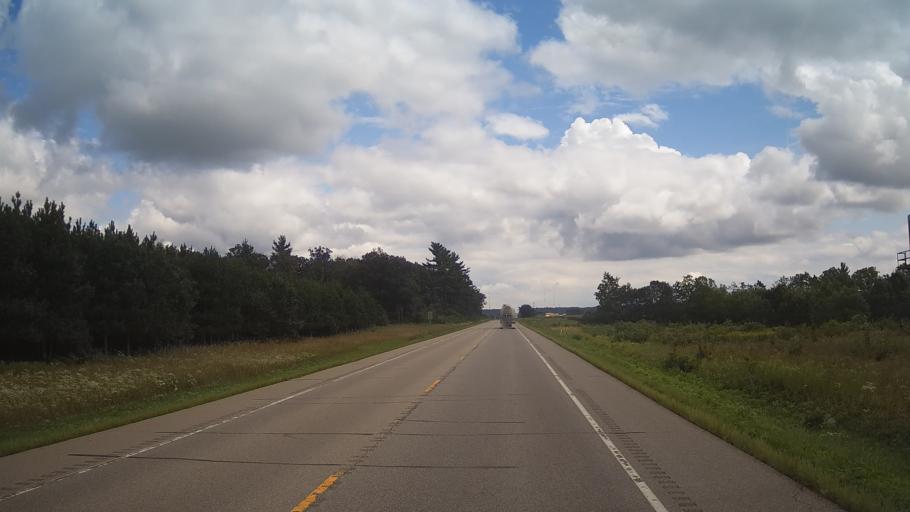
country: US
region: Wisconsin
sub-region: Marquette County
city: Westfield
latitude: 44.0221
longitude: -89.6156
